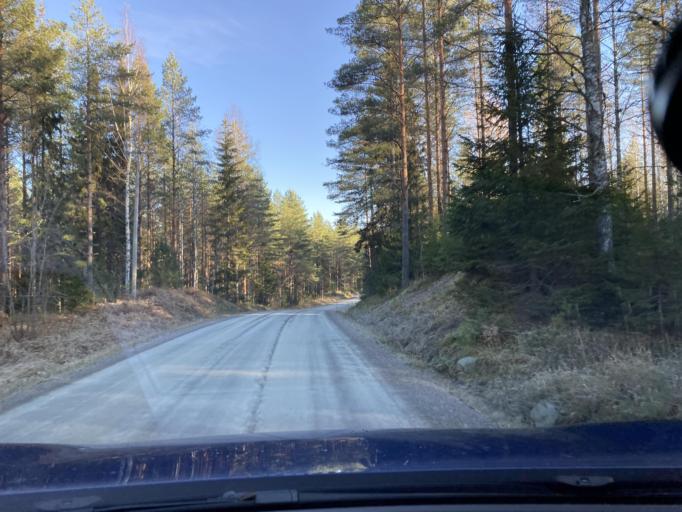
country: FI
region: Haeme
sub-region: Haemeenlinna
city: Kalvola
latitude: 60.9989
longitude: 24.1086
